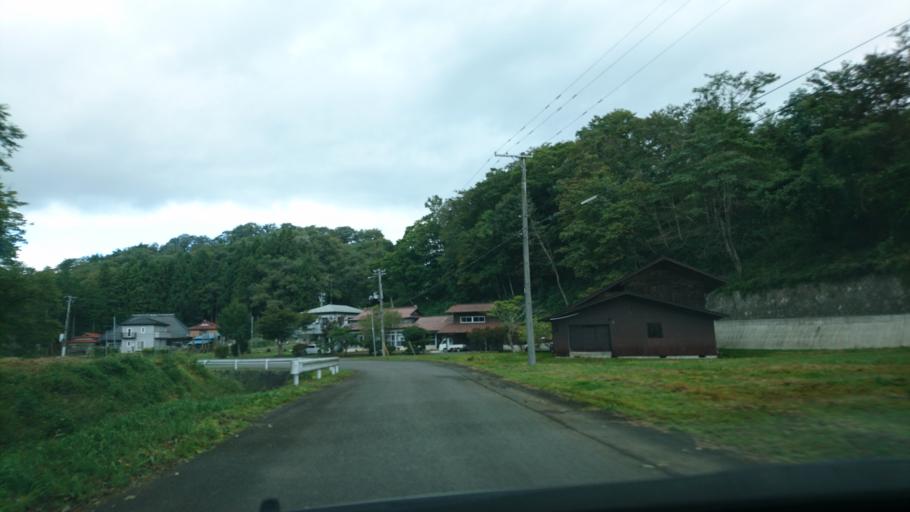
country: JP
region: Iwate
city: Ichinoseki
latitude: 38.8962
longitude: 141.0896
